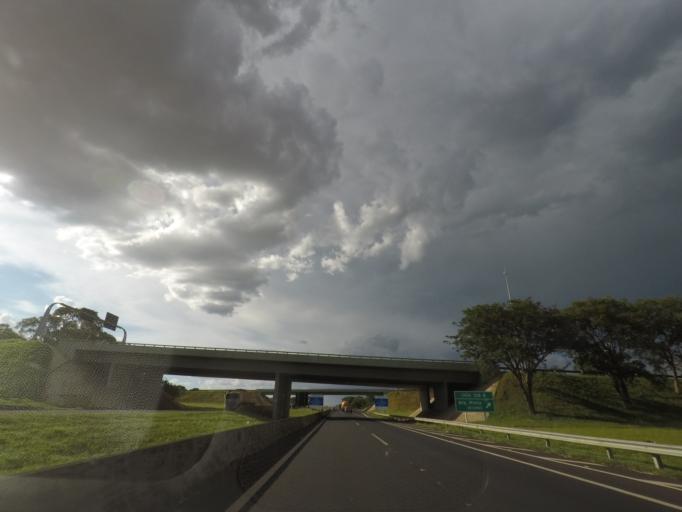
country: BR
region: Sao Paulo
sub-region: Ribeirao Preto
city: Ribeirao Preto
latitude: -21.1140
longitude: -47.7792
